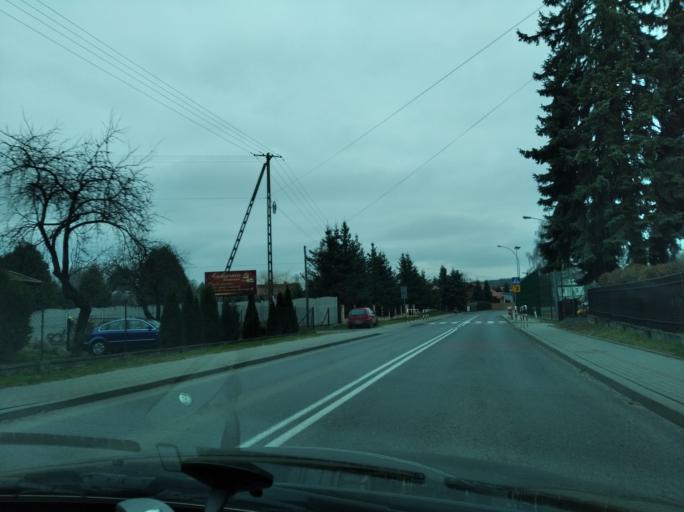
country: PL
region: Subcarpathian Voivodeship
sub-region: Powiat lancucki
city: Zolynia
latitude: 50.1650
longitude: 22.3095
